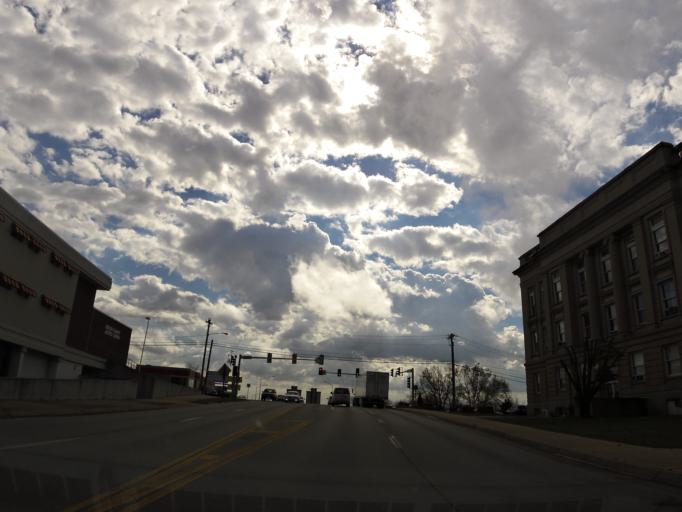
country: US
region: Missouri
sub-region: Butler County
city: Poplar Bluff
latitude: 36.7569
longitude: -90.3928
